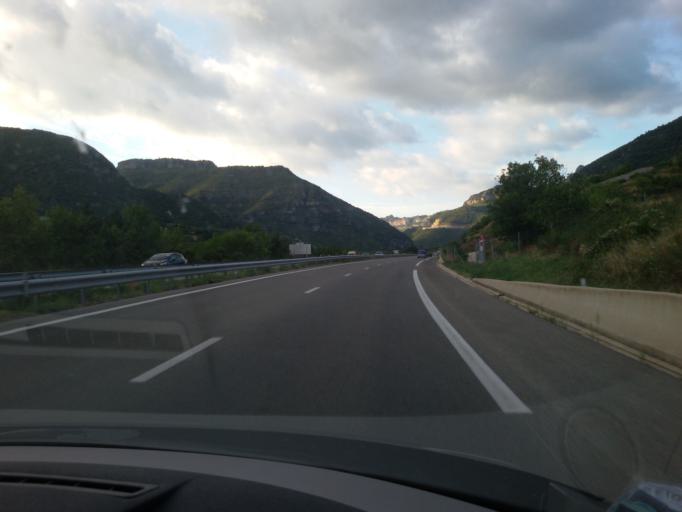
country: FR
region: Languedoc-Roussillon
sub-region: Departement de l'Herault
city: Lodeve
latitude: 43.7857
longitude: 3.3274
